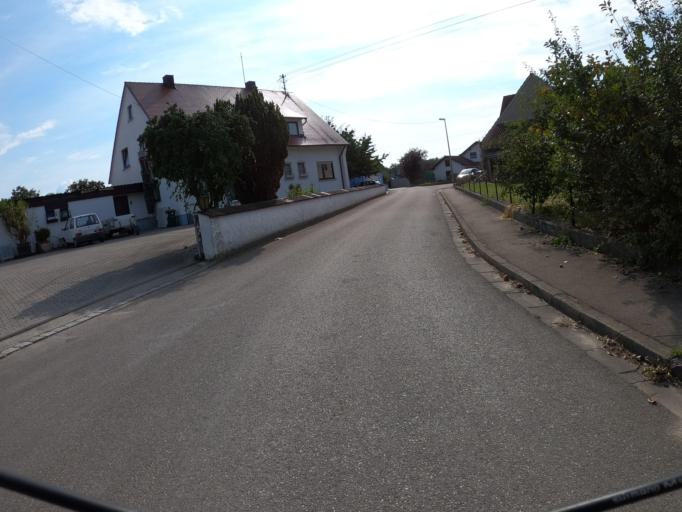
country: DE
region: Bavaria
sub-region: Swabia
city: Leipheim
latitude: 48.4253
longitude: 10.1959
